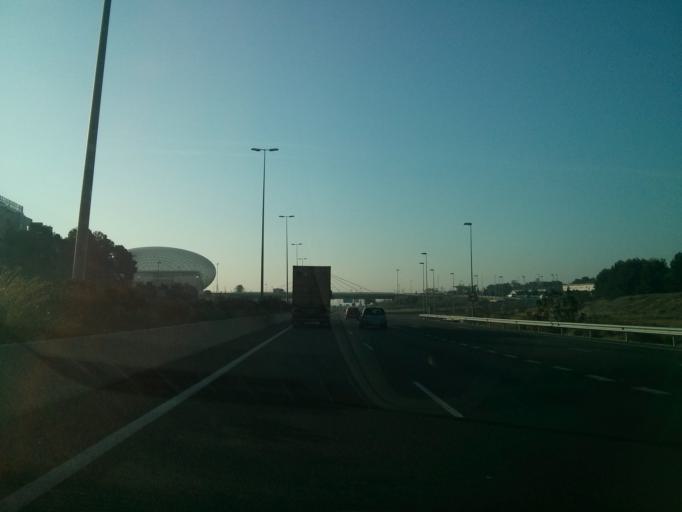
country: ES
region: Valencia
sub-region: Provincia de Valencia
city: Paterna
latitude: 39.5046
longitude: -0.4318
